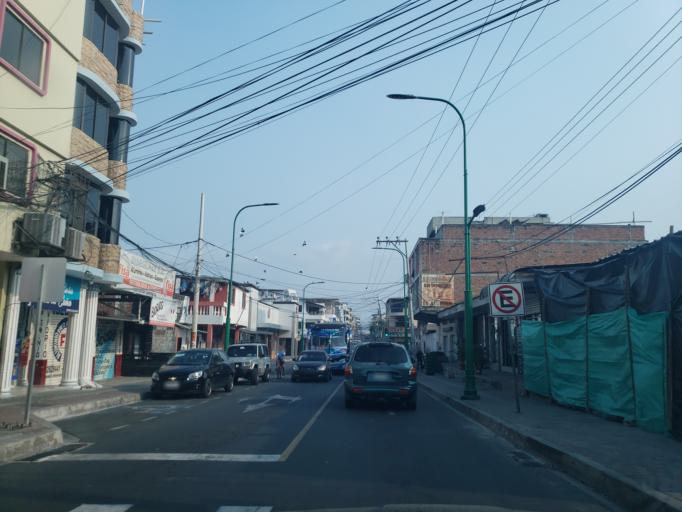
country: EC
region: Manabi
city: Manta
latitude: -0.9495
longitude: -80.7313
